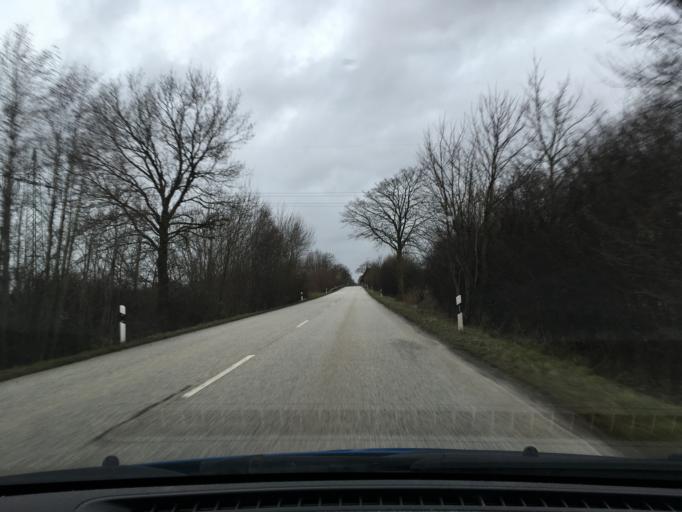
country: DE
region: Schleswig-Holstein
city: Kruzen
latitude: 53.3926
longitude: 10.5422
